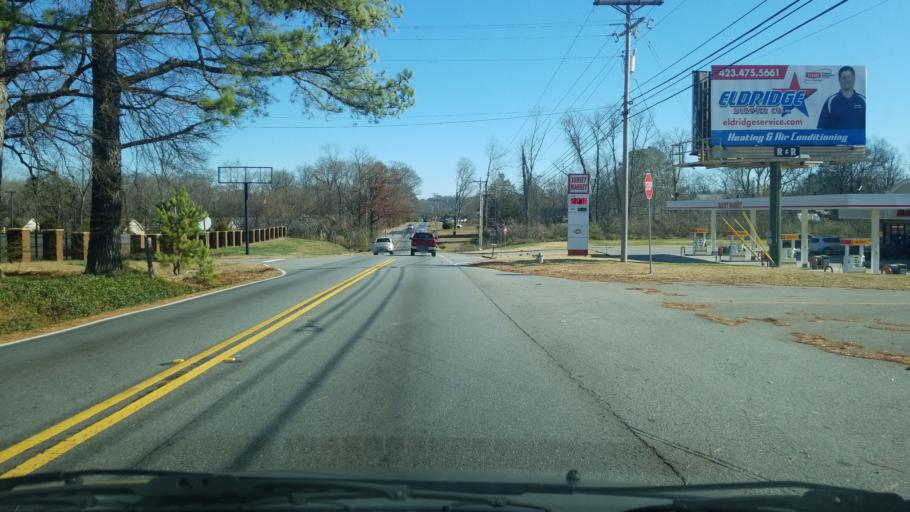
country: US
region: Georgia
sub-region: Catoosa County
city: Fort Oglethorpe
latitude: 34.9570
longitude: -85.2334
